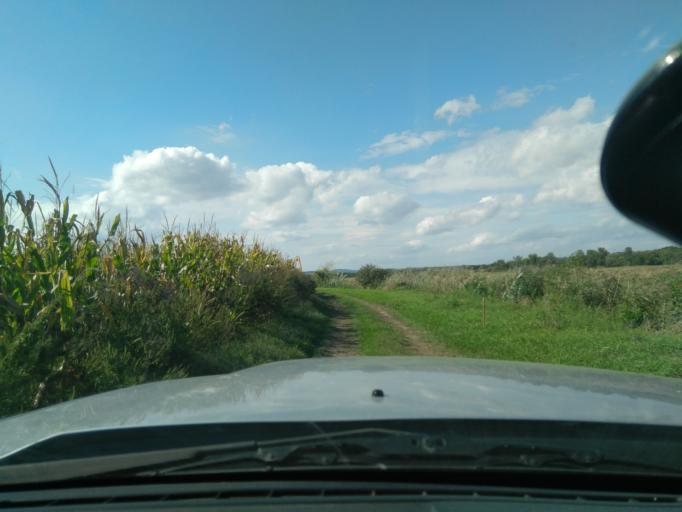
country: HU
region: Fejer
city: Bicske
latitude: 47.4805
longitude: 18.6663
